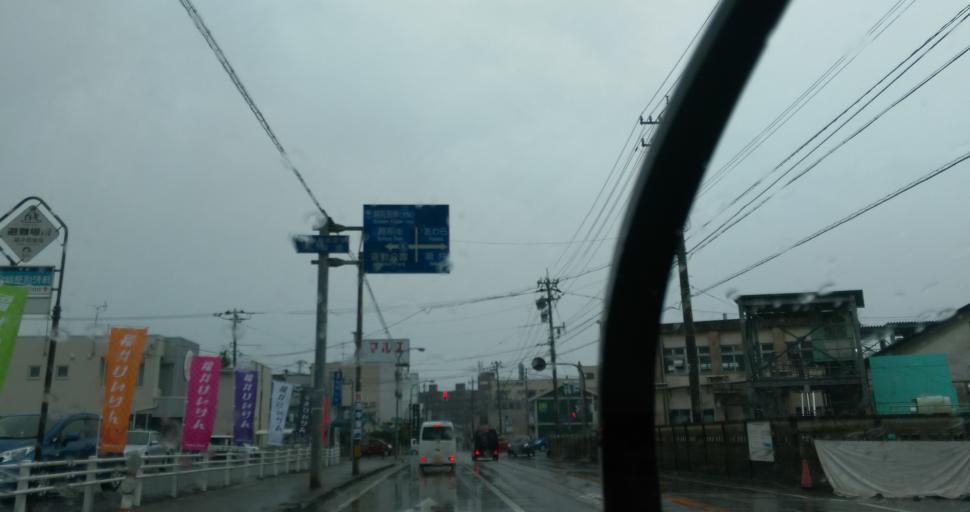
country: JP
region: Fukui
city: Fukui-shi
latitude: 36.0617
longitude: 136.1984
